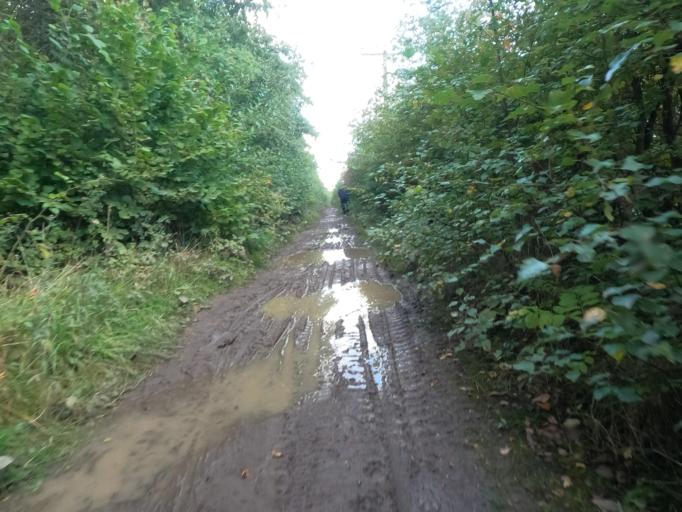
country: GB
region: England
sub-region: Northumberland
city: Seghill
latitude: 55.0706
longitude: -1.5473
